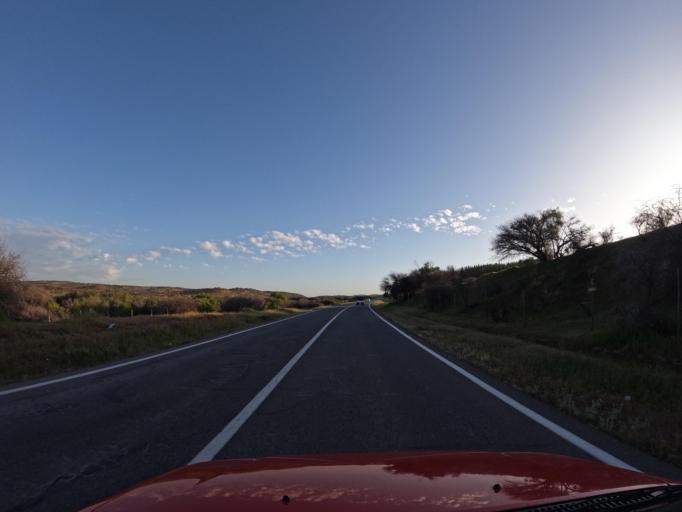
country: CL
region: O'Higgins
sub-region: Provincia de Colchagua
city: Santa Cruz
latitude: -34.2968
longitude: -71.7320
